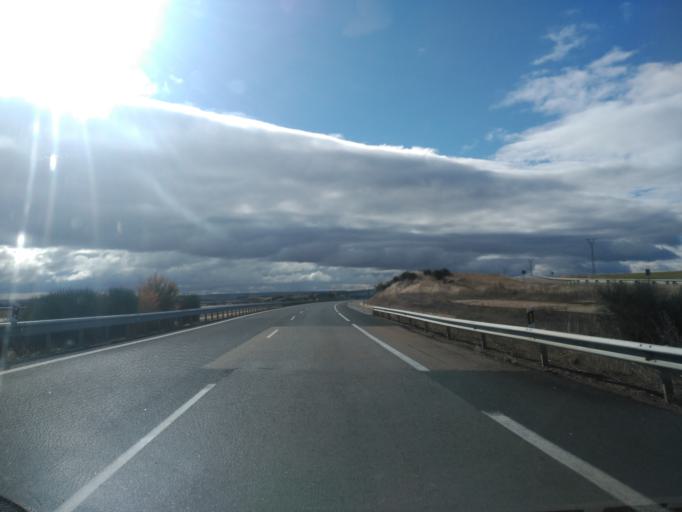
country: ES
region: Castille and Leon
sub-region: Provincia de Palencia
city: Fromista
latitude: 42.2848
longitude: -4.4007
